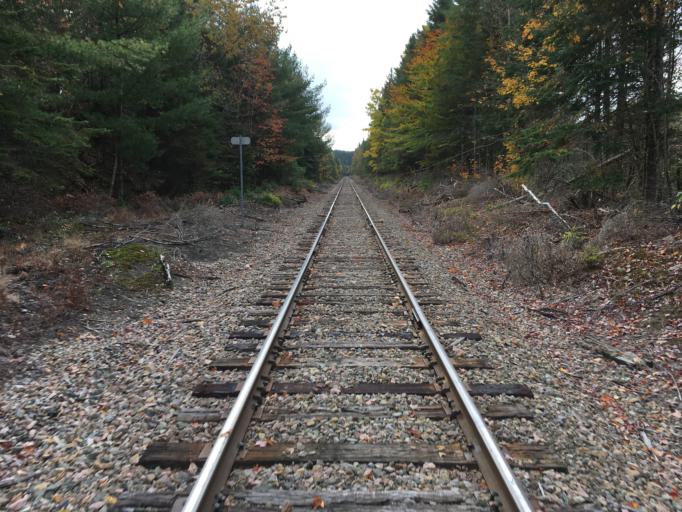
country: US
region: Vermont
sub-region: Caledonia County
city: Lyndonville
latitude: 44.6238
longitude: -71.9672
